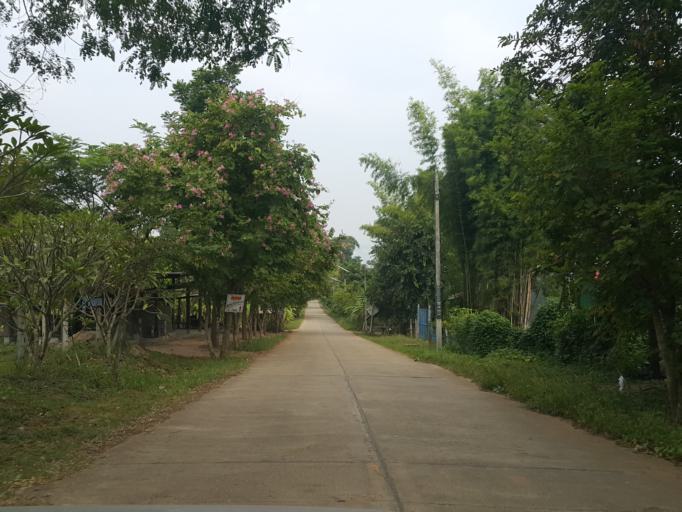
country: TH
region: Mae Hong Son
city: Wiang Nuea
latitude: 19.3697
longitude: 98.4490
